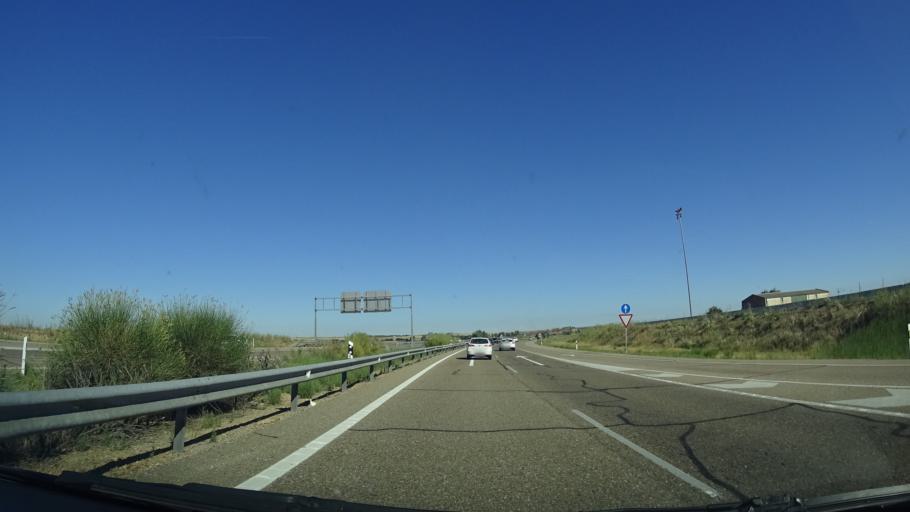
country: ES
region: Castille and Leon
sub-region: Provincia de Zamora
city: Villalpando
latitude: 41.8580
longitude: -5.4243
